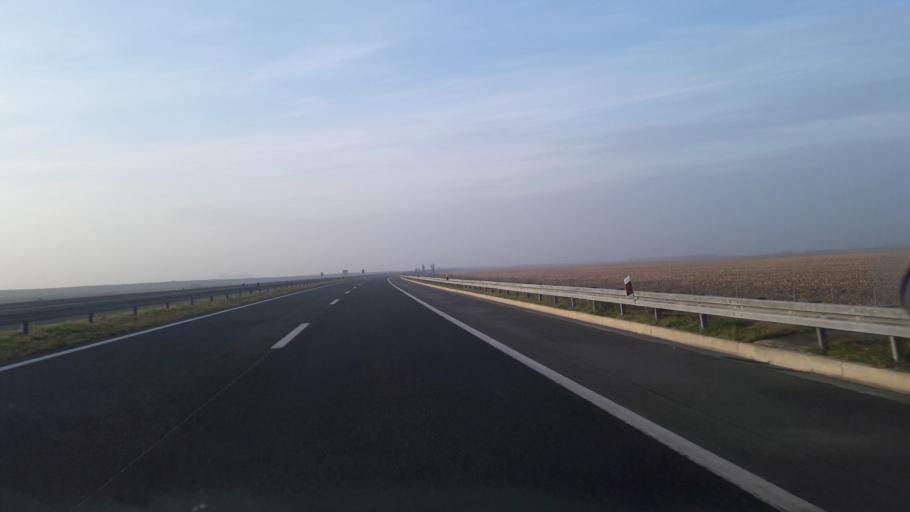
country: HR
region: Osjecko-Baranjska
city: Cepin
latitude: 45.5581
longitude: 18.5435
